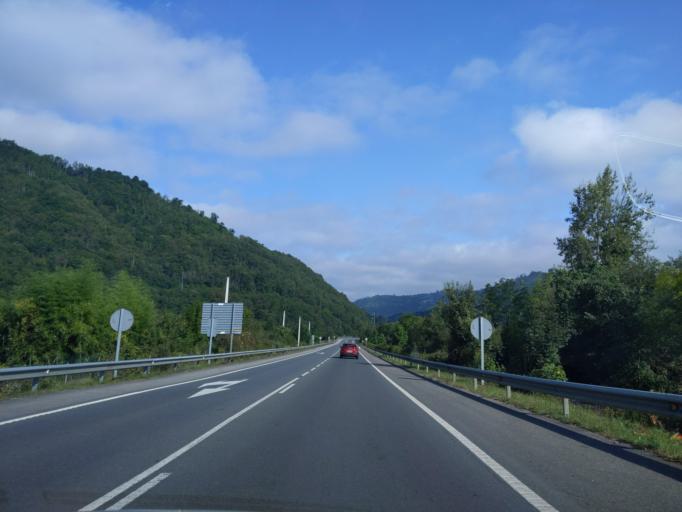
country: ES
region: Asturias
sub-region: Province of Asturias
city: Pola de Laviana
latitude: 43.2525
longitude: -5.5709
